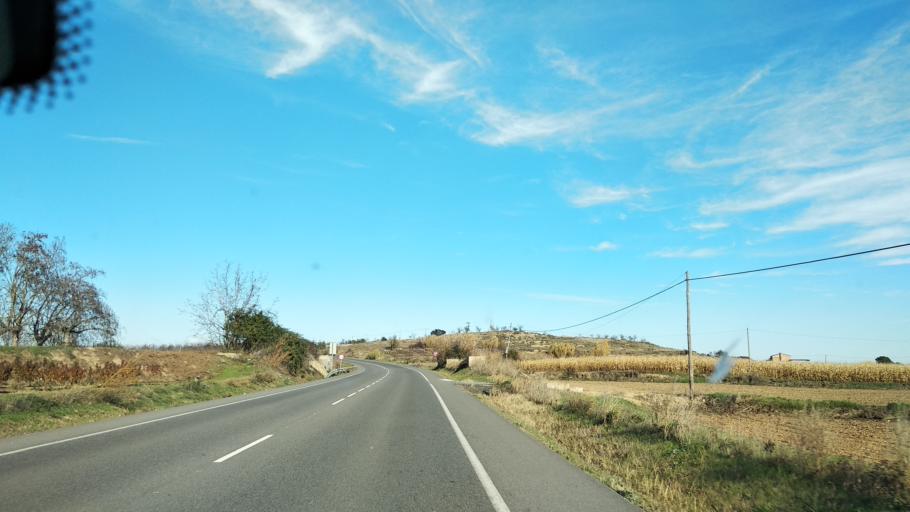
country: ES
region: Catalonia
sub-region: Provincia de Lleida
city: Alcoletge
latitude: 41.6669
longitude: 0.6667
